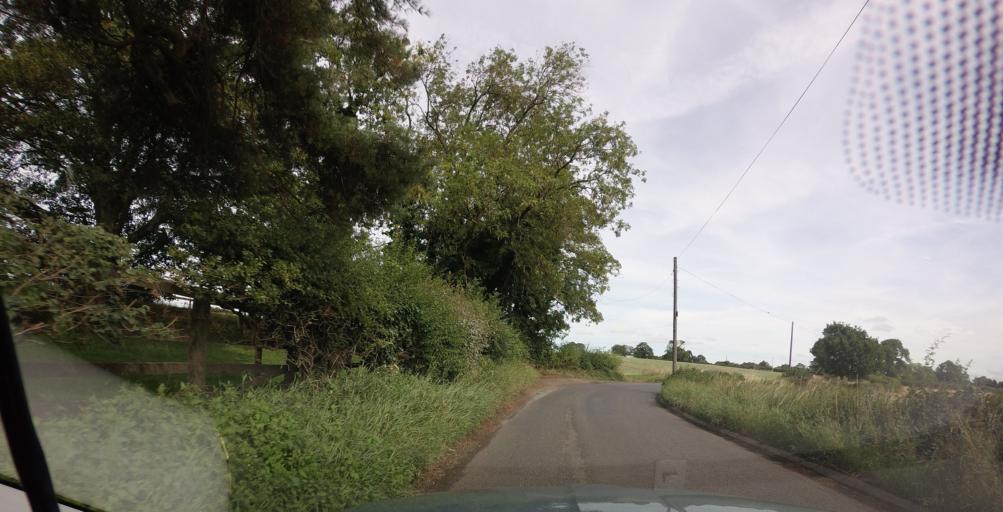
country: GB
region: England
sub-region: North Yorkshire
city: Ripon
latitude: 54.1089
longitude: -1.5164
